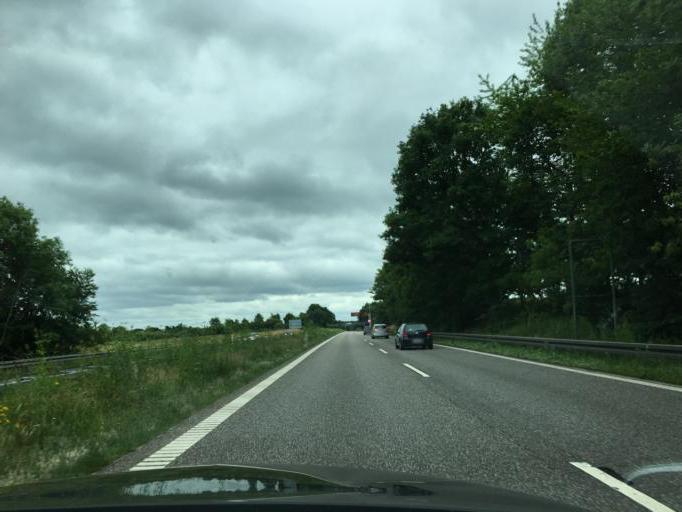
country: DK
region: Capital Region
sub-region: Fredensborg Kommune
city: Kokkedal
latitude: 55.8963
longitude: 12.4751
